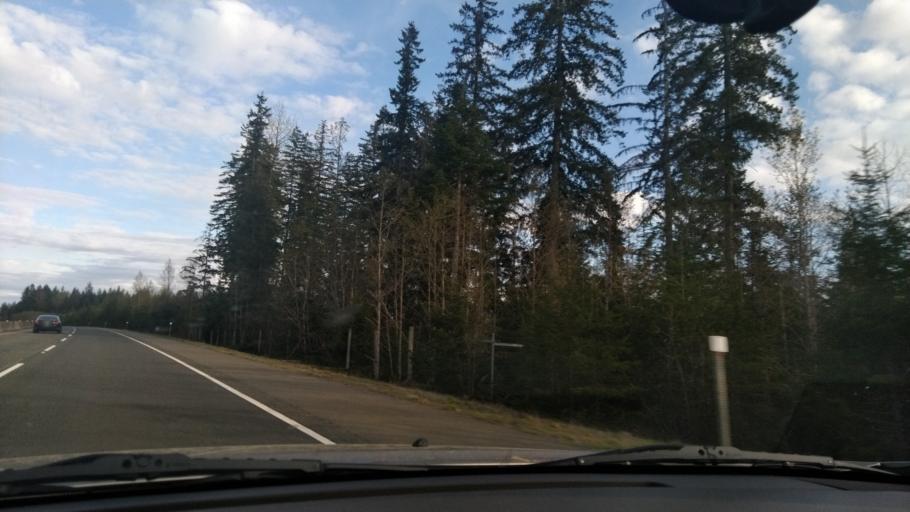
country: CA
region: British Columbia
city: Campbell River
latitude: 49.8314
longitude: -125.1909
